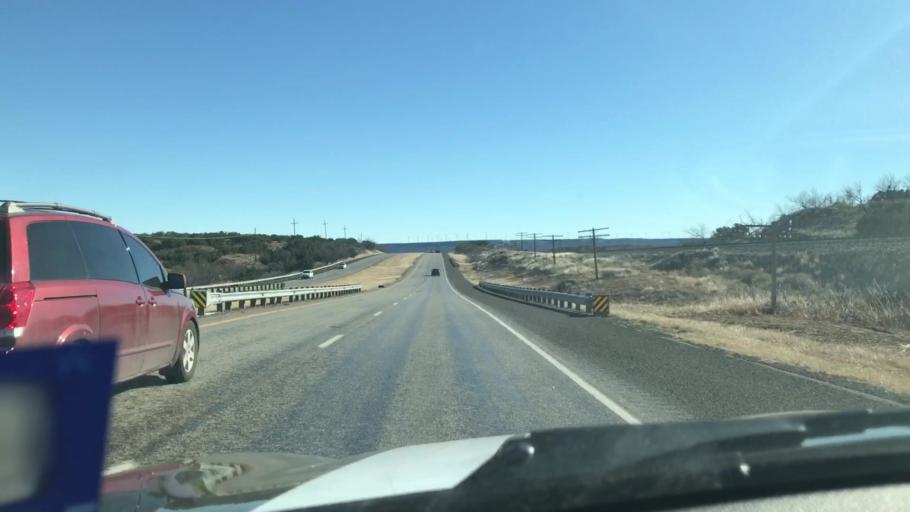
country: US
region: Texas
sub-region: Garza County
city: Post
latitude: 33.0251
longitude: -101.1838
